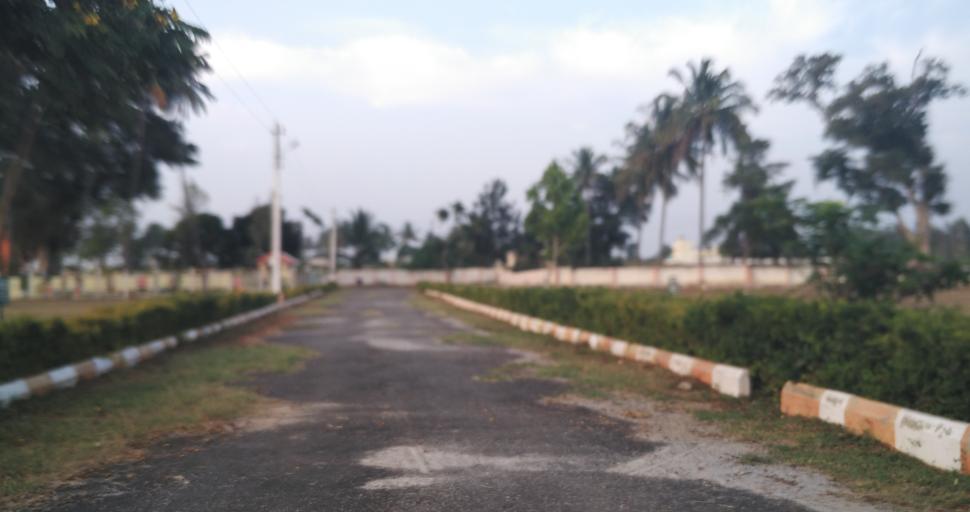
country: IN
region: Tamil Nadu
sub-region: Krishnagiri
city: Hosur
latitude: 12.6706
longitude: 77.8265
